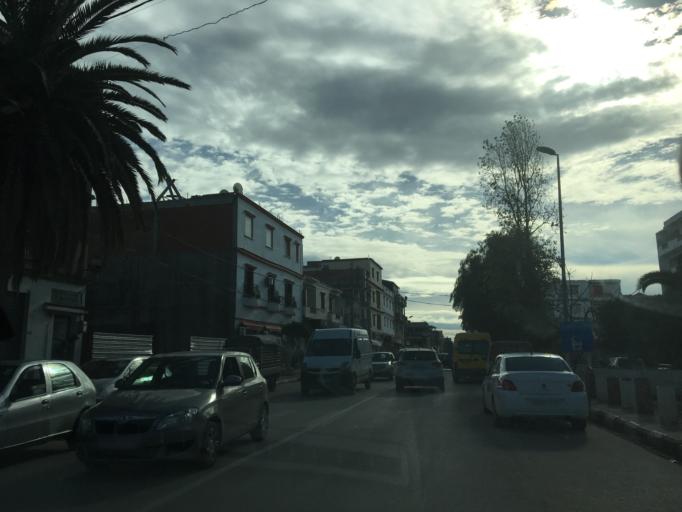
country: DZ
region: Alger
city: Ain Taya
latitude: 36.7883
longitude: 3.2497
